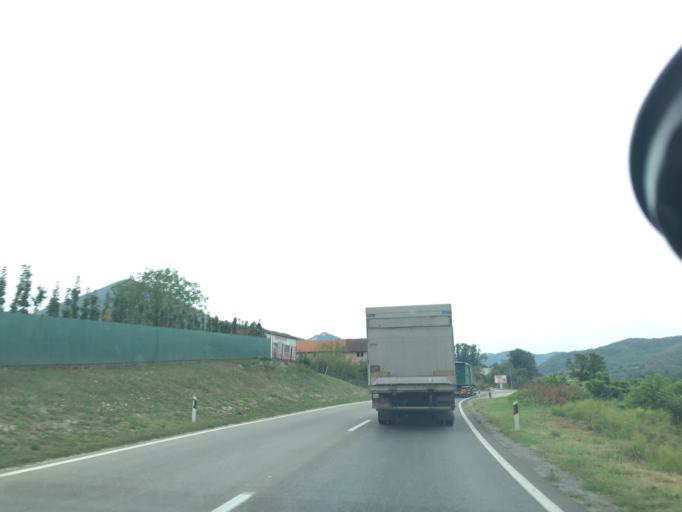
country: RS
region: Central Serbia
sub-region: Moravicki Okrug
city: Cacak
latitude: 43.8988
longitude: 20.2657
